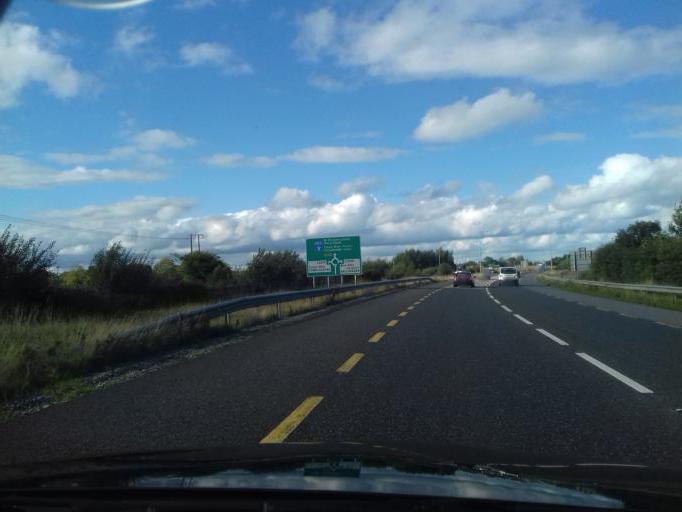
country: IE
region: Leinster
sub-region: Uibh Fhaili
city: Tullamore
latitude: 53.2748
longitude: -7.4669
